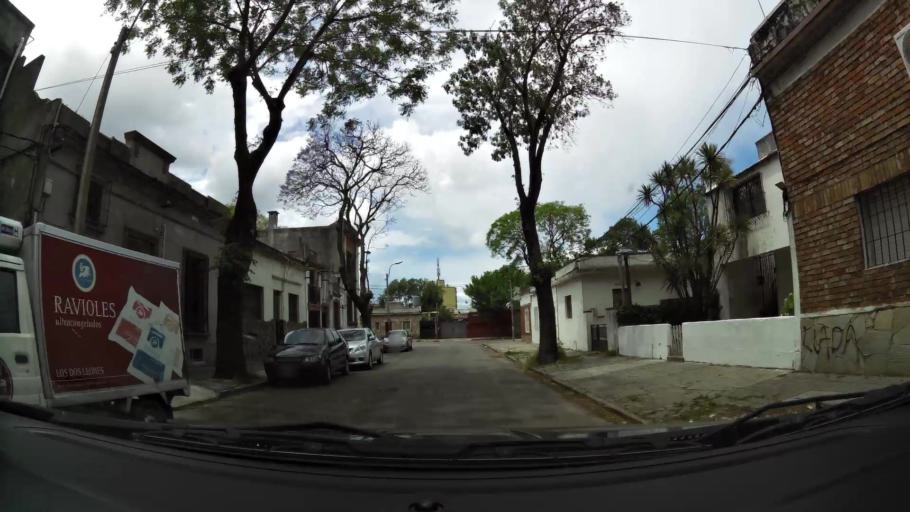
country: UY
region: Montevideo
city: Montevideo
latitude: -34.8844
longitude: -56.1470
